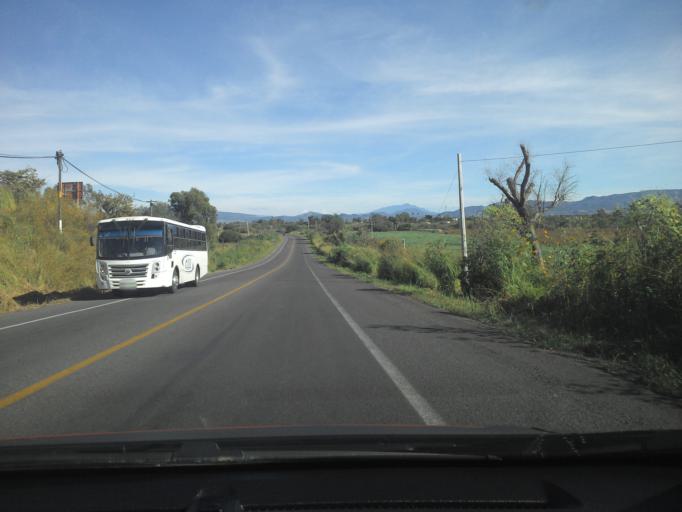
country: MX
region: Jalisco
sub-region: Teuchitlan
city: La Estanzuela
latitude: 20.6766
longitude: -103.8350
